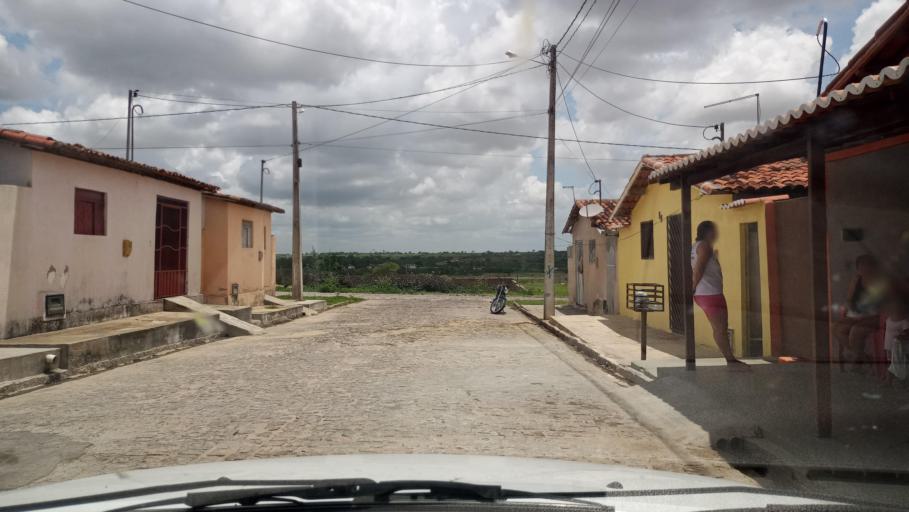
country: BR
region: Rio Grande do Norte
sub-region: Tangara
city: Tangara
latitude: -6.0979
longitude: -35.7094
